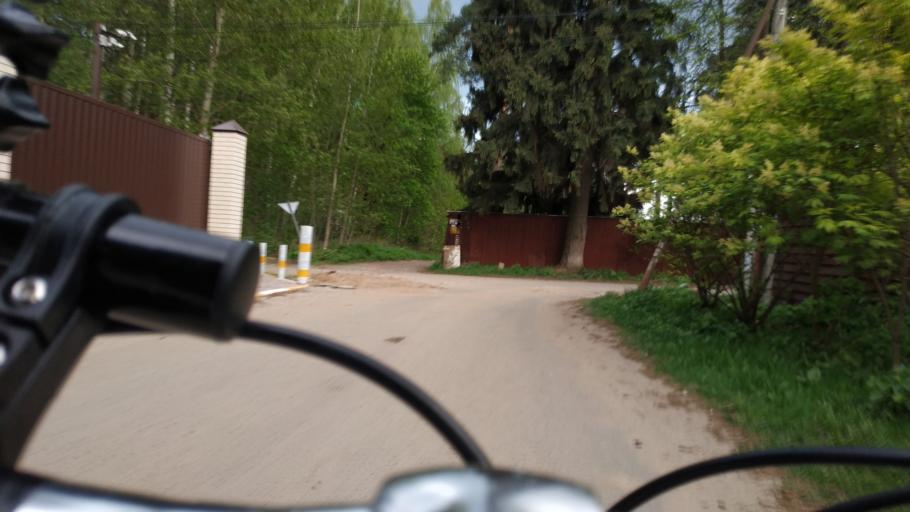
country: RU
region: Moskovskaya
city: Kratovo
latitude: 55.6057
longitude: 38.1757
